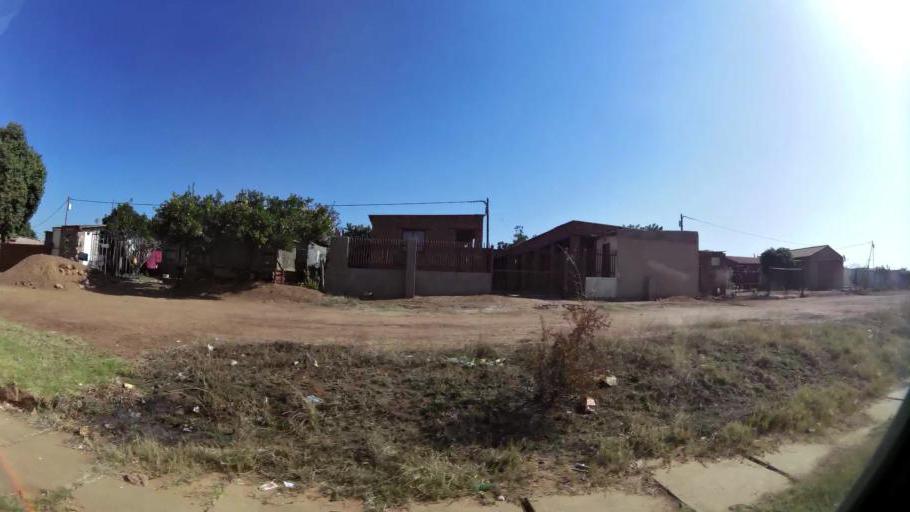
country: ZA
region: Gauteng
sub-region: City of Tshwane Metropolitan Municipality
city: Mabopane
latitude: -25.5523
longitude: 28.1017
